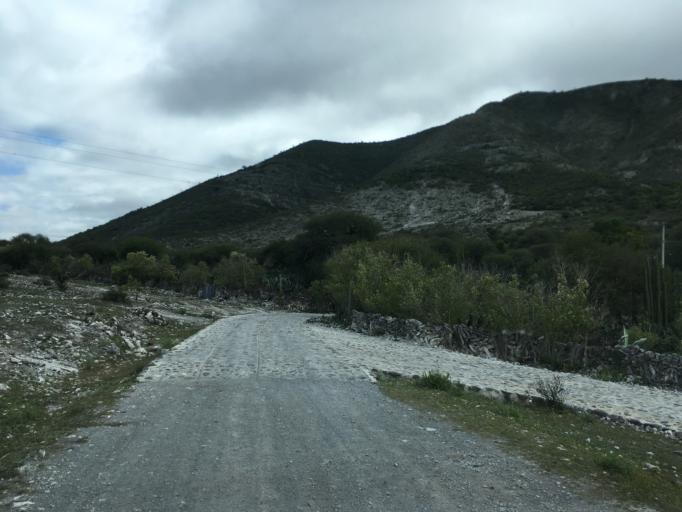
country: MX
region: Hidalgo
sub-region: Metztitlan
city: Fontezuelas
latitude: 20.6250
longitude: -98.8602
